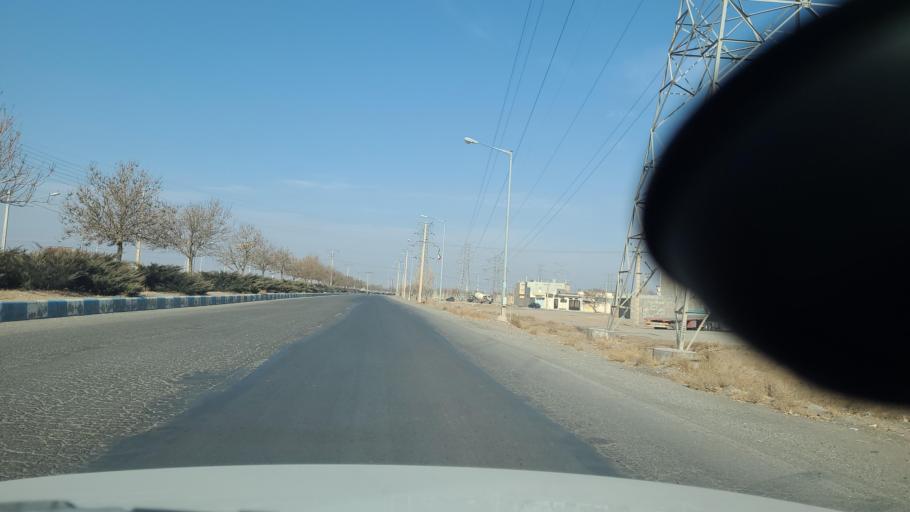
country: IR
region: Razavi Khorasan
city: Fariman
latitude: 35.7017
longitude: 59.8357
